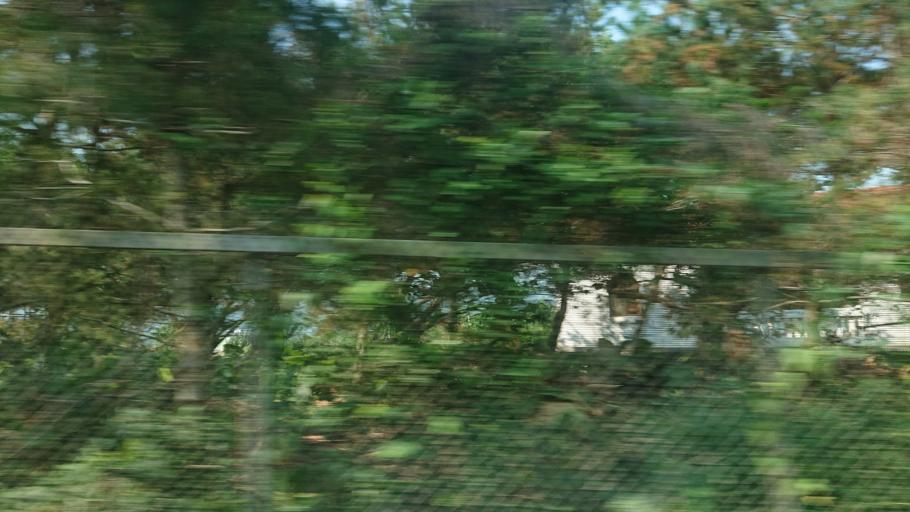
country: TW
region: Taiwan
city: Lugu
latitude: 23.6913
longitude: 120.6634
